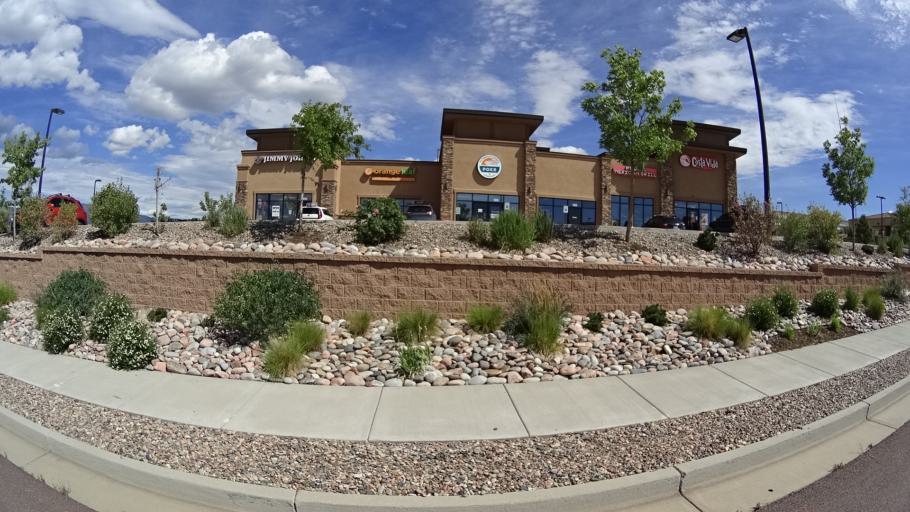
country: US
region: Colorado
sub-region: El Paso County
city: Gleneagle
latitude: 39.0258
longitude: -104.8238
